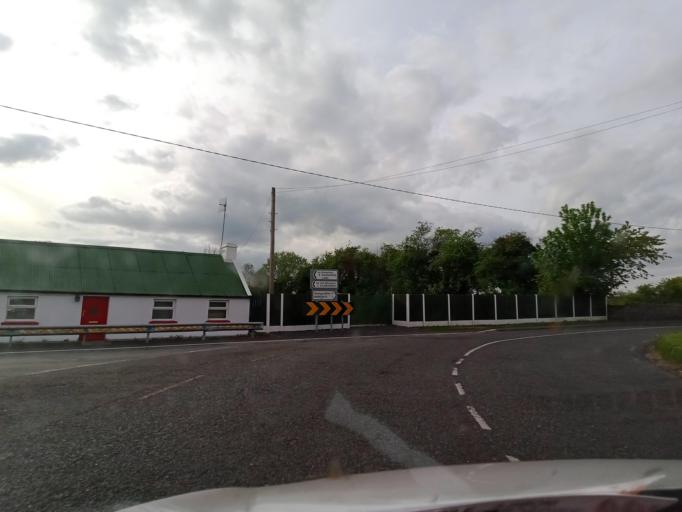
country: IE
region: Leinster
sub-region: Laois
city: Mountrath
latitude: 52.9908
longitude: -7.4692
